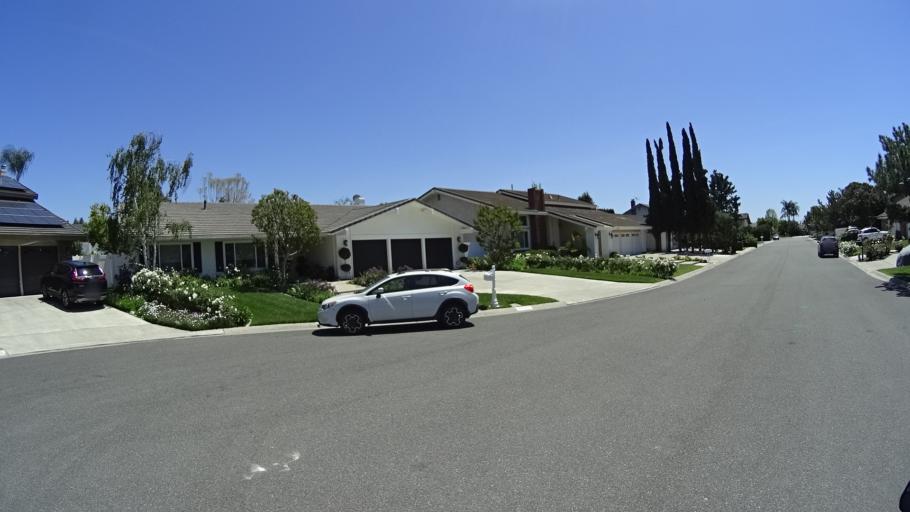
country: US
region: California
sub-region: Orange County
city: Villa Park
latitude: 33.8092
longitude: -117.8212
